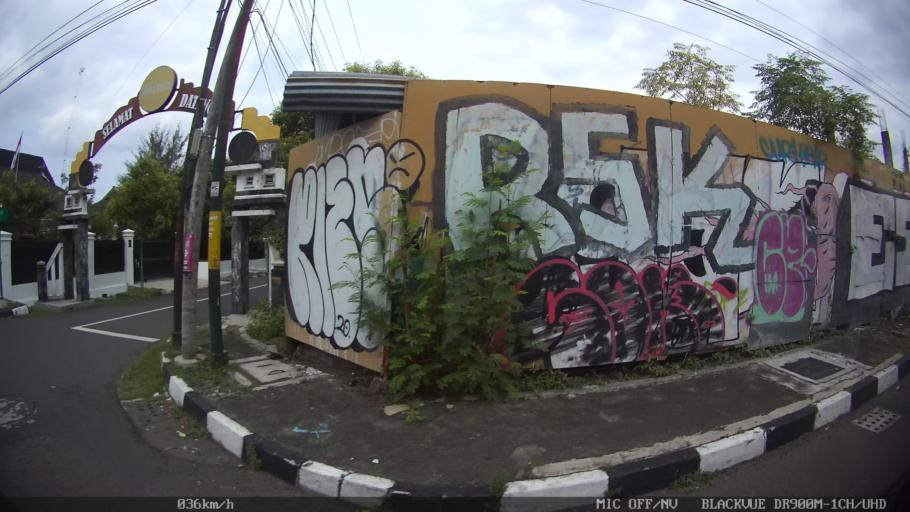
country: ID
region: Daerah Istimewa Yogyakarta
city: Yogyakarta
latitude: -7.7909
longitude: 110.3830
